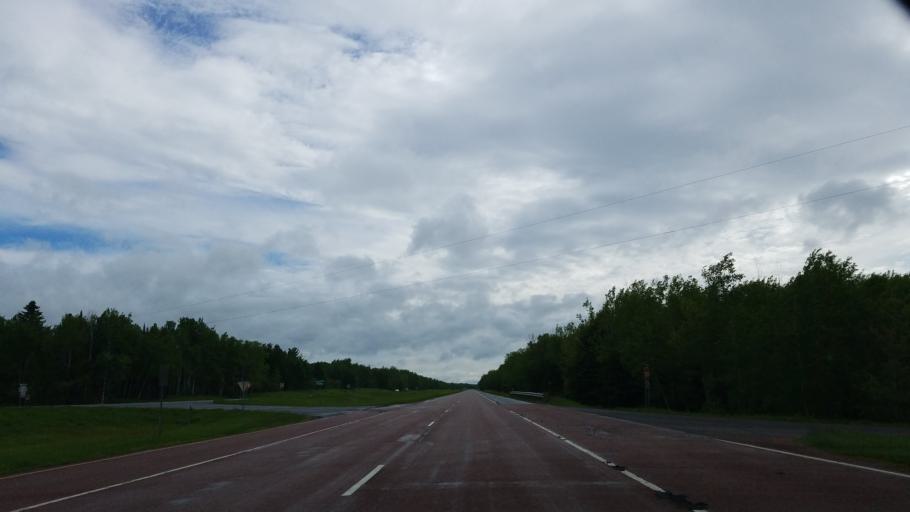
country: US
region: Minnesota
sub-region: Saint Louis County
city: Arnold
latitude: 46.8712
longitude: -91.9535
